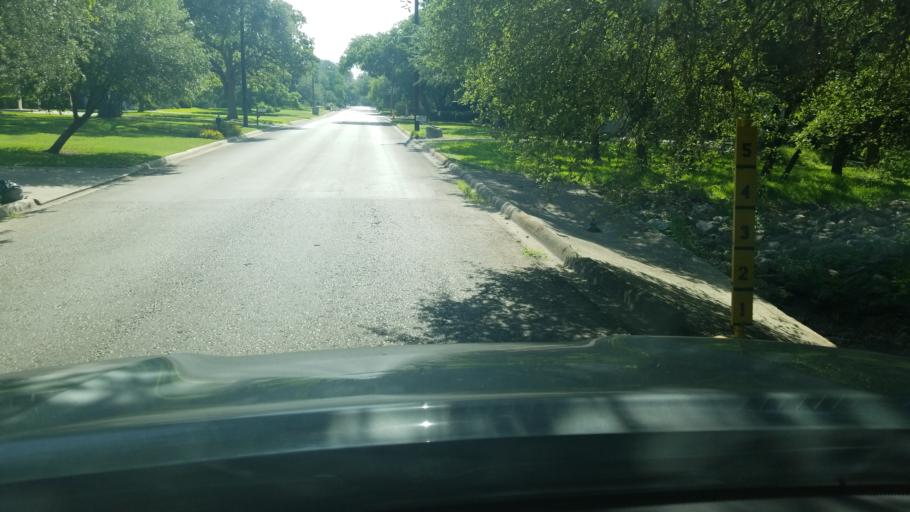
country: US
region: Texas
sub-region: Bexar County
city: Hollywood Park
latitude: 29.6039
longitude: -98.4820
